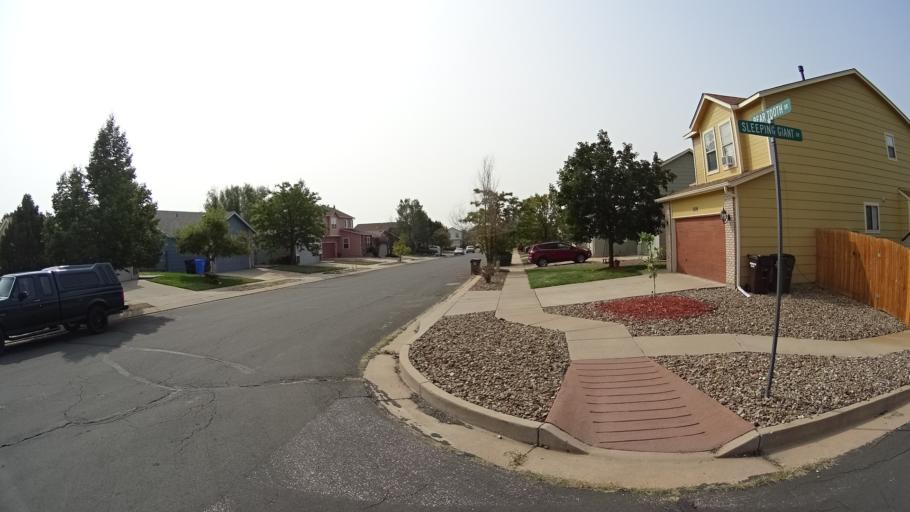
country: US
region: Colorado
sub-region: El Paso County
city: Cimarron Hills
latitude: 38.9275
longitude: -104.7292
